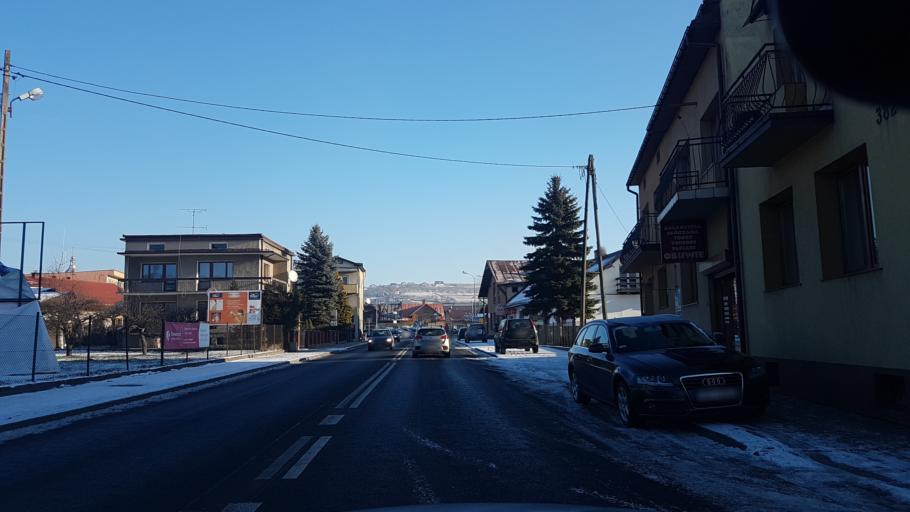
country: PL
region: Lesser Poland Voivodeship
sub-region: Powiat nowosadecki
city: Lacko
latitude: 49.5565
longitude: 20.4338
